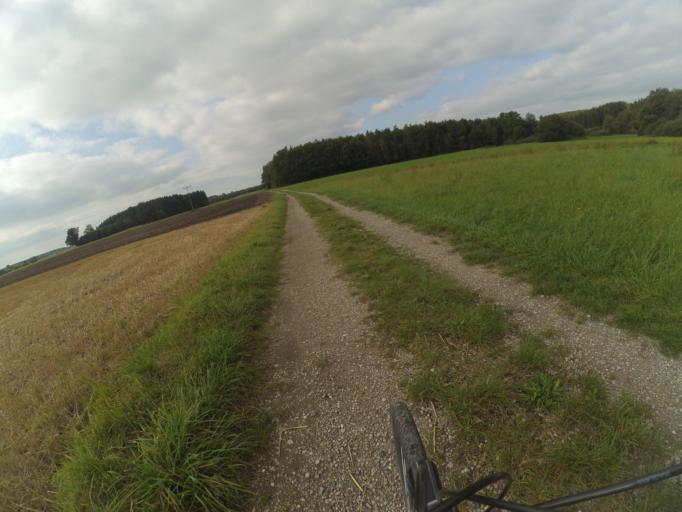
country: DE
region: Bavaria
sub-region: Swabia
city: Lamerdingen
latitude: 48.0588
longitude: 10.7879
